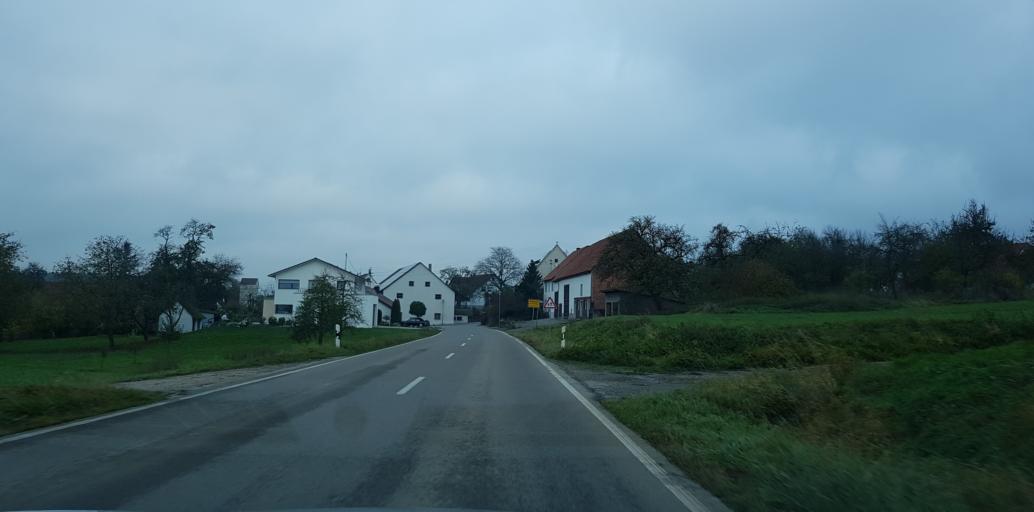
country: DE
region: Baden-Wuerttemberg
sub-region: Tuebingen Region
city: Altheim
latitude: 48.3101
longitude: 9.7894
